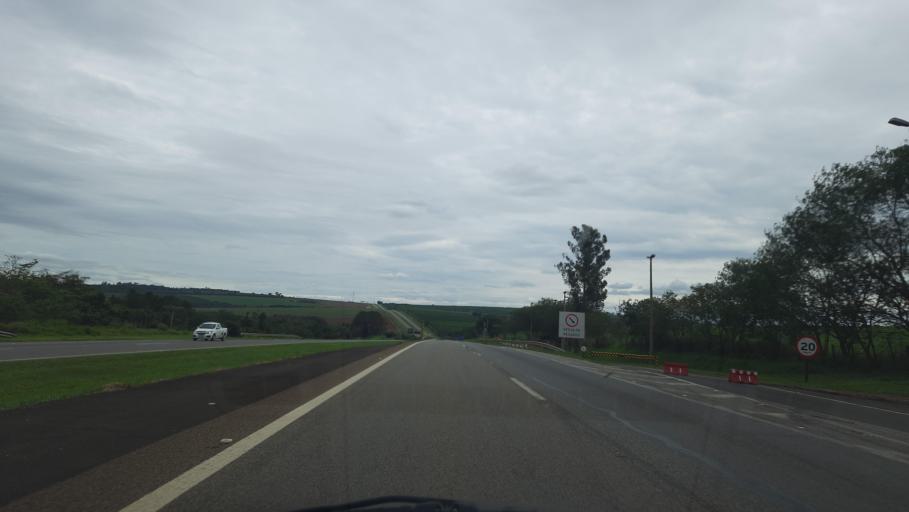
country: BR
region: Sao Paulo
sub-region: Aguai
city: Aguai
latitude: -22.1147
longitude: -47.0023
